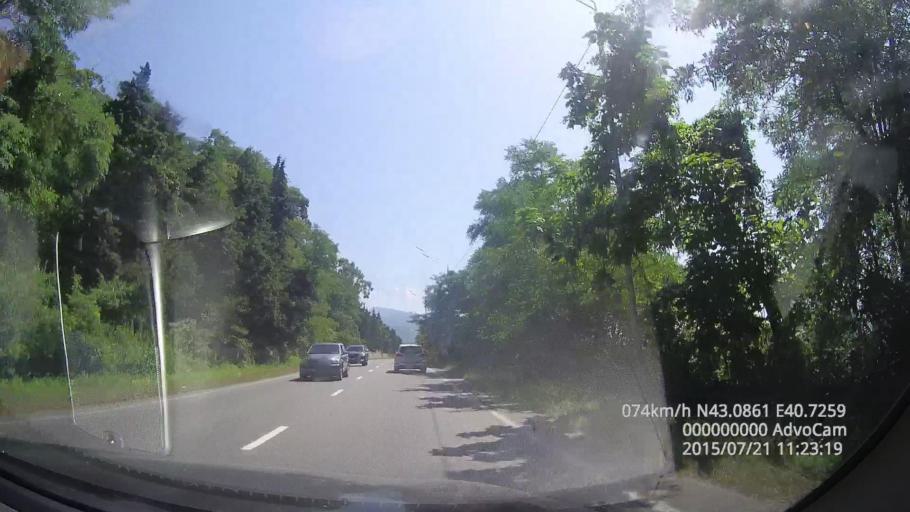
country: GE
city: P'rimorsk'oe
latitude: 43.0862
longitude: 40.7263
